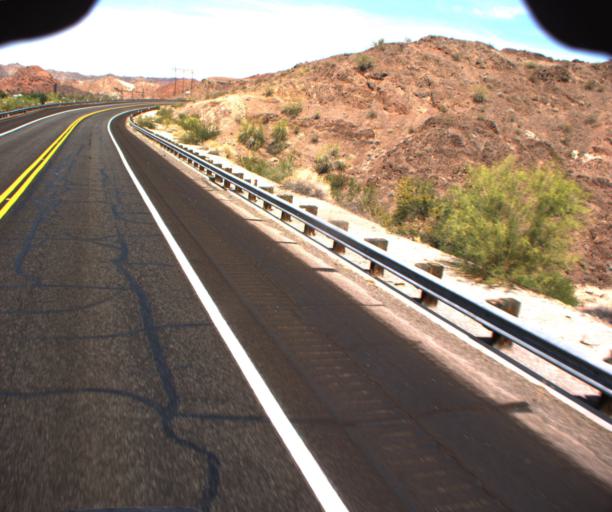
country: US
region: Arizona
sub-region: La Paz County
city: Cienega Springs
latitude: 34.2377
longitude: -114.1768
